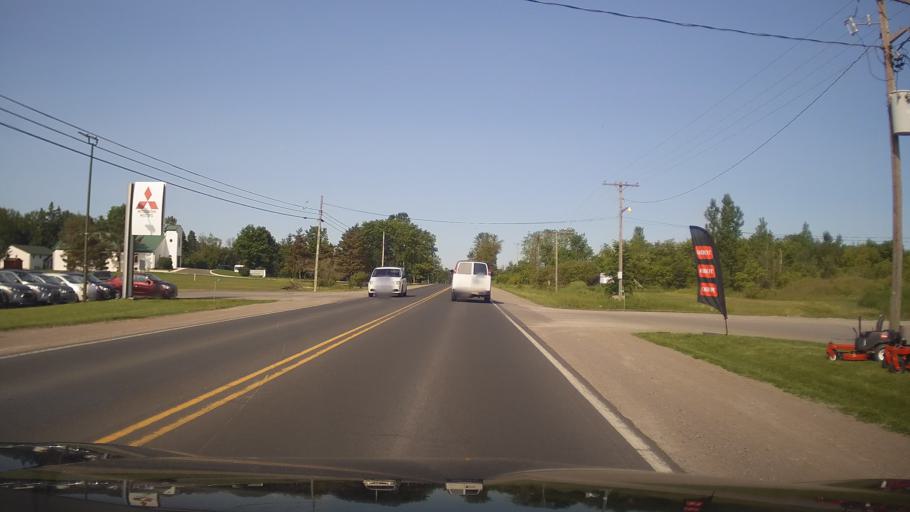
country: CA
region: Ontario
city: Peterborough
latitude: 44.2729
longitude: -78.3835
